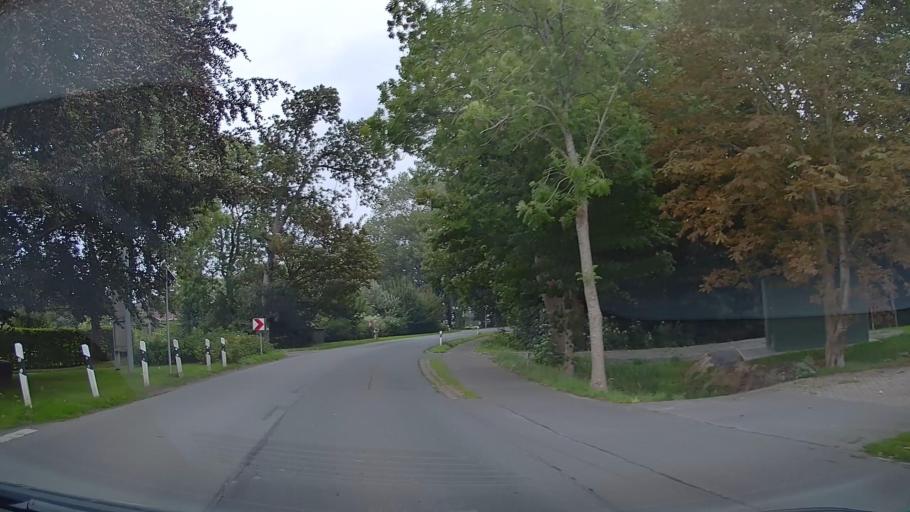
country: DE
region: Lower Saxony
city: Geversdorf
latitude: 53.8211
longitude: 9.0897
